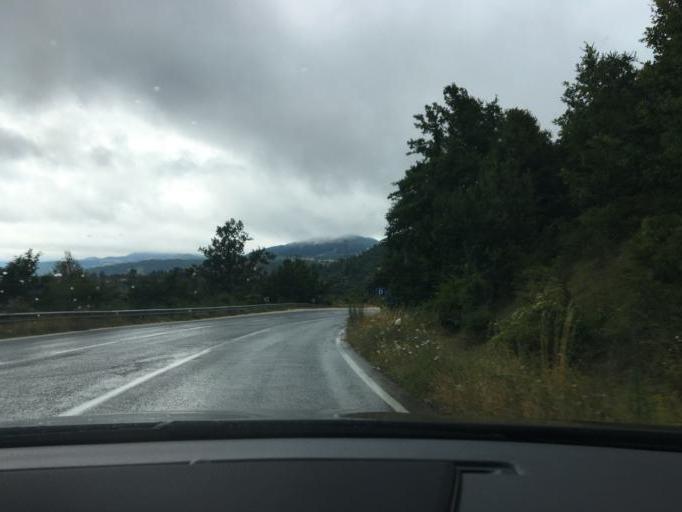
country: MK
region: Kriva Palanka
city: Kriva Palanka
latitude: 42.2182
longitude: 22.4447
